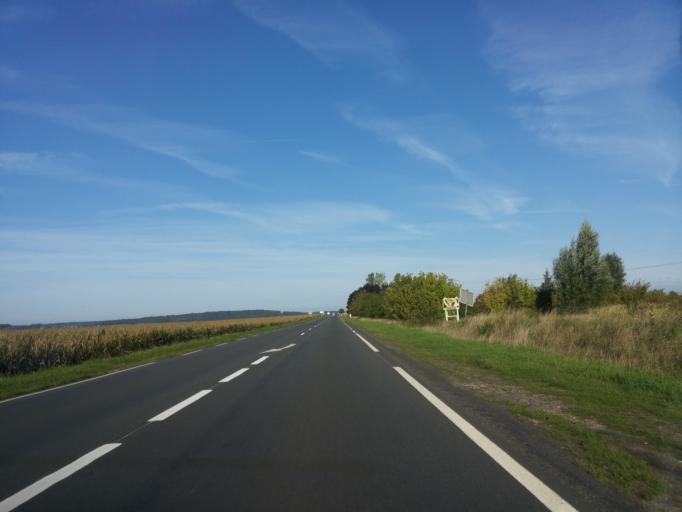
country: FR
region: Picardie
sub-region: Departement de l'Aisne
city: Laon
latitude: 49.5796
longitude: 3.5782
